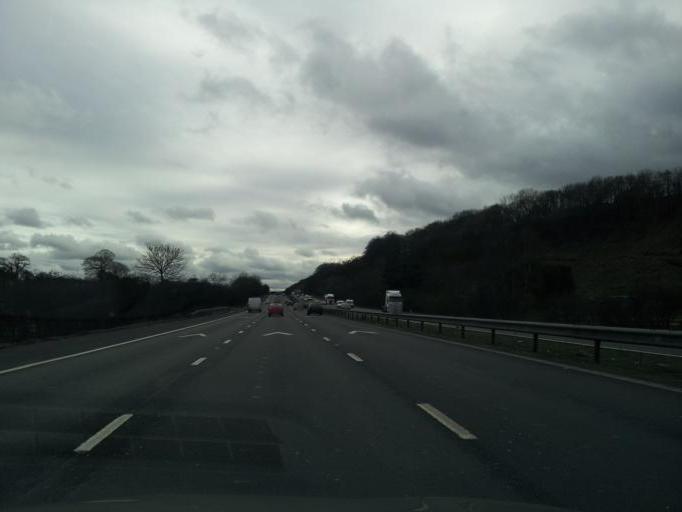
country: GB
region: England
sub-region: Staffordshire
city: Barlaston
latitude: 52.9503
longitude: -2.2179
